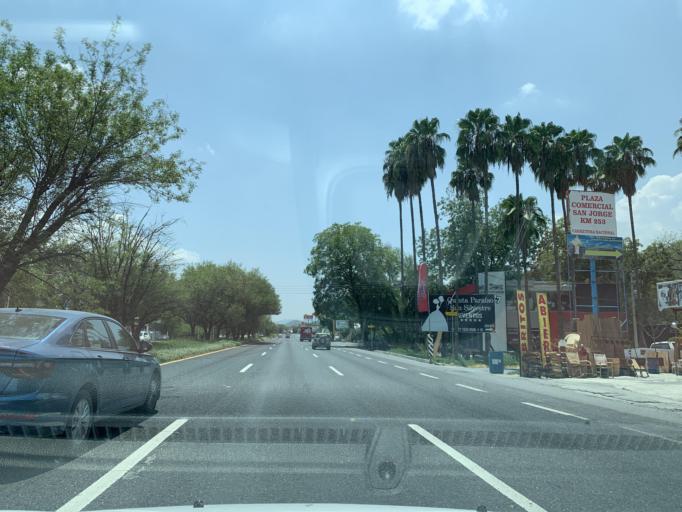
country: MX
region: Nuevo Leon
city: Santiago
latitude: 25.4645
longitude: -100.1723
